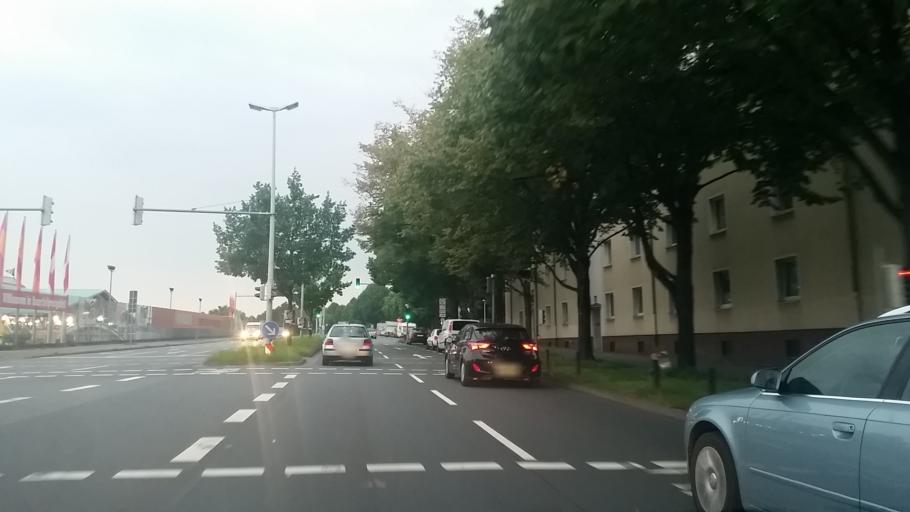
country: DE
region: Lower Saxony
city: Hannover
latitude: 52.3604
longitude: 9.7105
